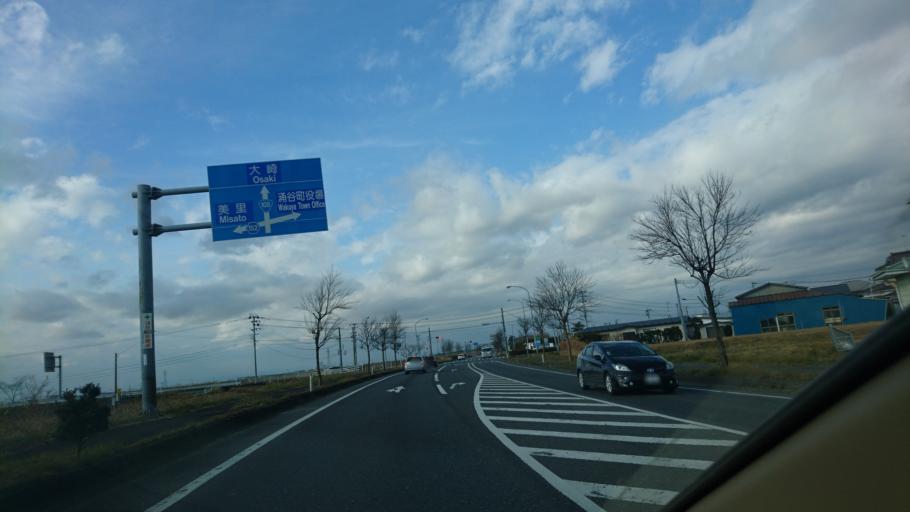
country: JP
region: Miyagi
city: Wakuya
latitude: 38.5333
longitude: 141.1230
